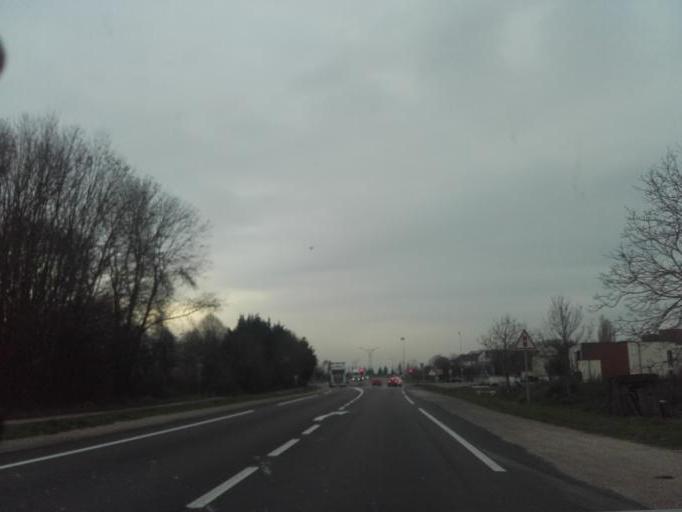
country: FR
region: Bourgogne
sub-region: Departement de la Cote-d'Or
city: Beaune
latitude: 47.0110
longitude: 4.8534
